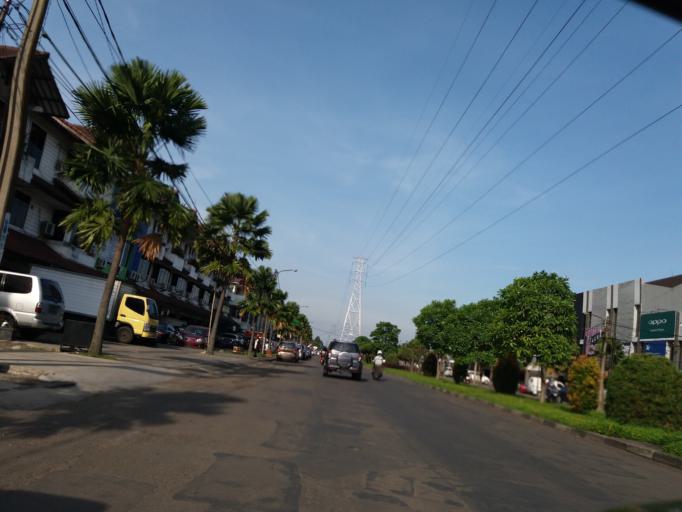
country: ID
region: West Java
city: Bandung
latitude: -6.9543
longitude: 107.6296
